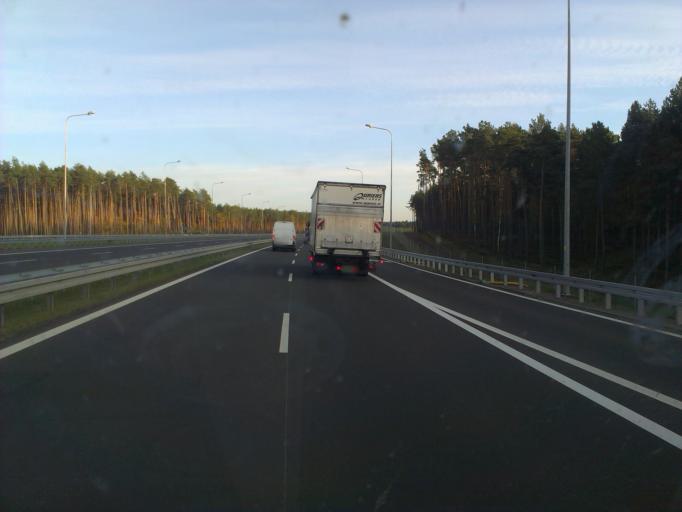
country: PL
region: Lubusz
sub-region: Powiat miedzyrzecki
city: Skwierzyna
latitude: 52.5591
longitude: 15.5298
